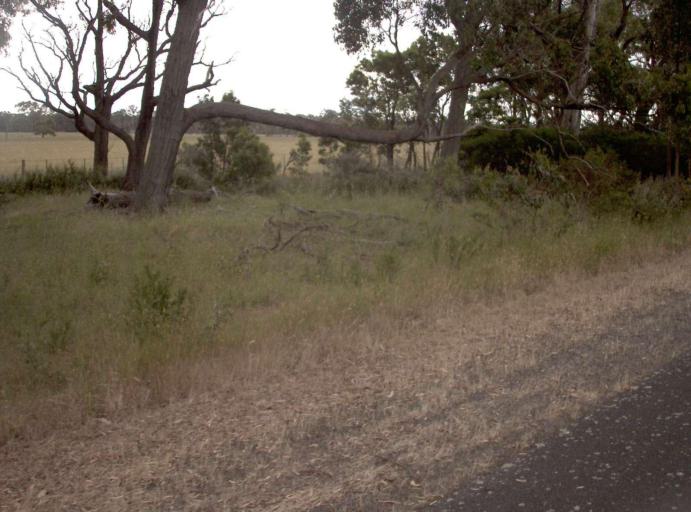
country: AU
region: Victoria
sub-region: Wellington
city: Sale
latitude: -38.4771
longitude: 146.9233
